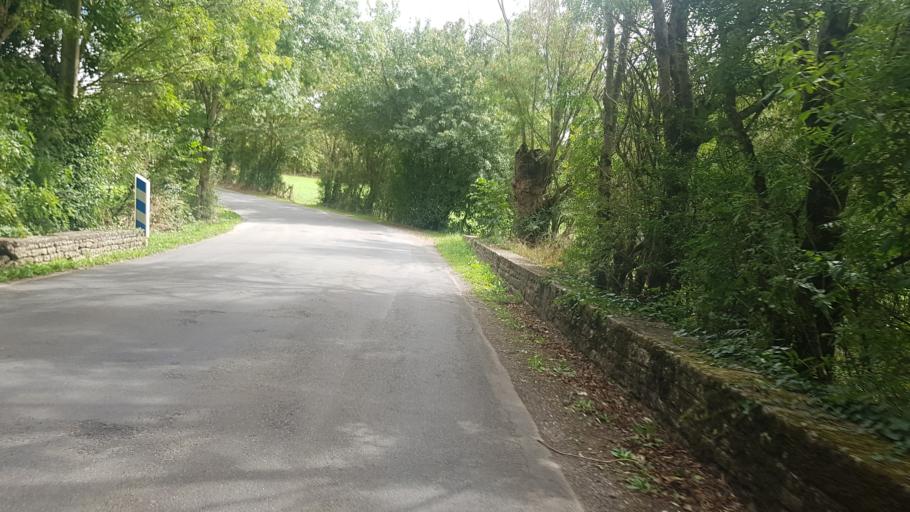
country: FR
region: Poitou-Charentes
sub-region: Departement des Deux-Sevres
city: Vouille
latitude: 46.3311
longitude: -0.3644
